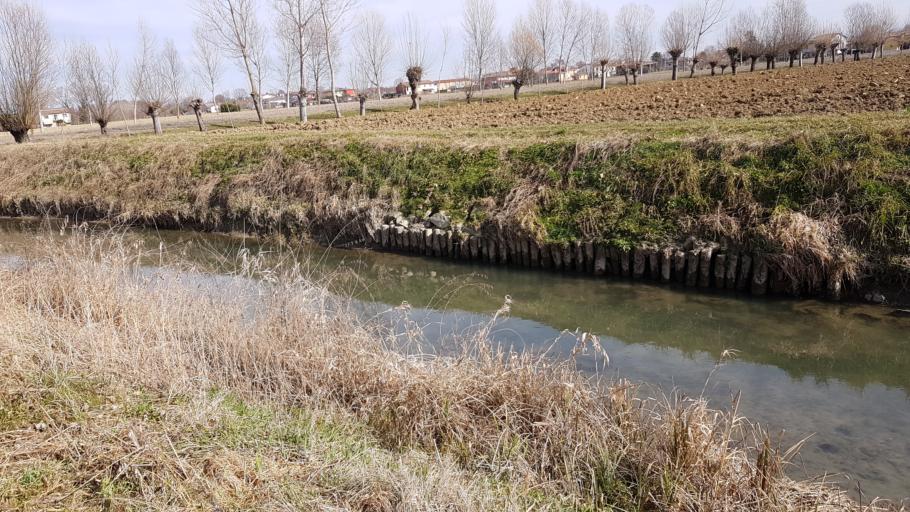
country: IT
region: Veneto
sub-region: Provincia di Padova
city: San Giorgio delle Pertiche
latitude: 45.5520
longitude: 11.9059
